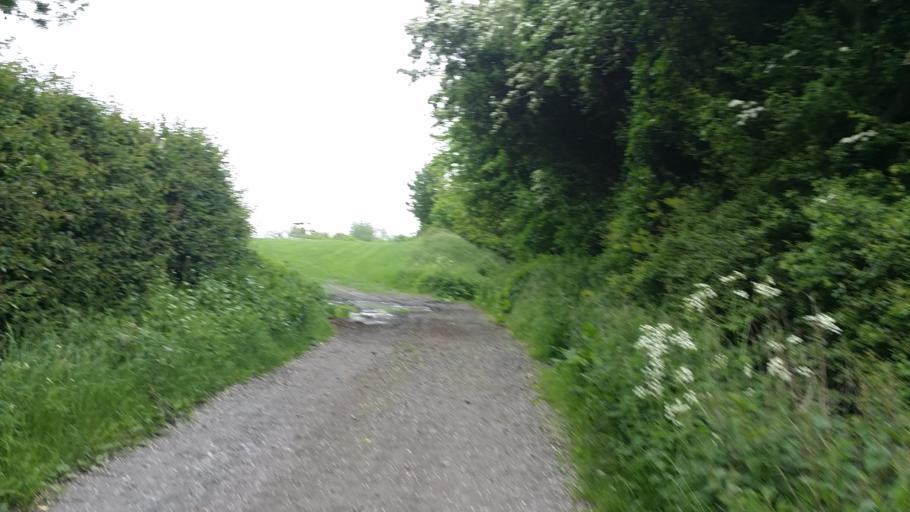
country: GB
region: England
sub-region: Sheffield
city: Chapletown
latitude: 53.4873
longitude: -1.4857
